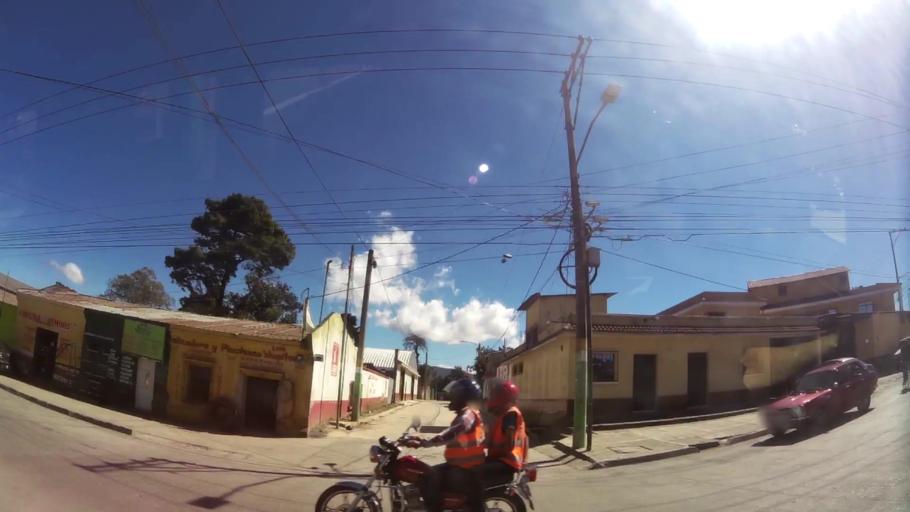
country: GT
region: Guatemala
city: San Jose Pinula
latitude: 14.5432
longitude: -90.4090
